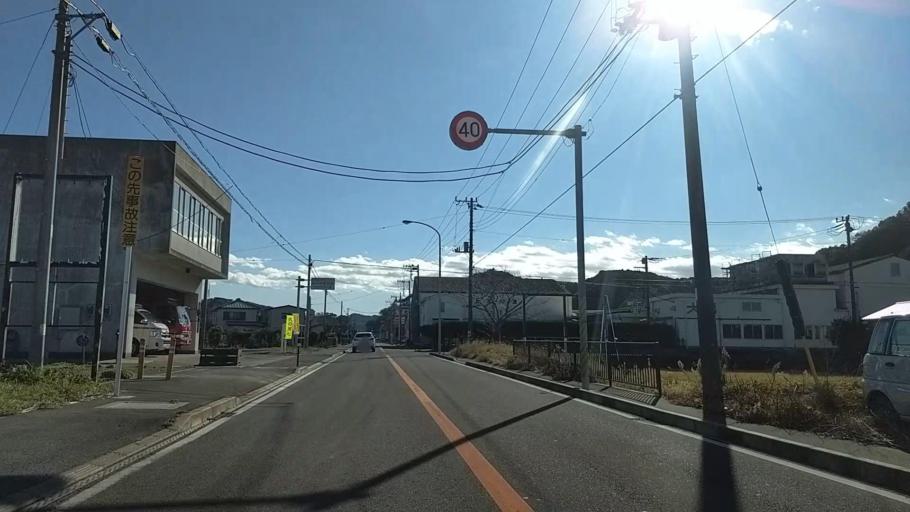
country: JP
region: Chiba
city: Tateyama
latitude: 35.1072
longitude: 139.8389
